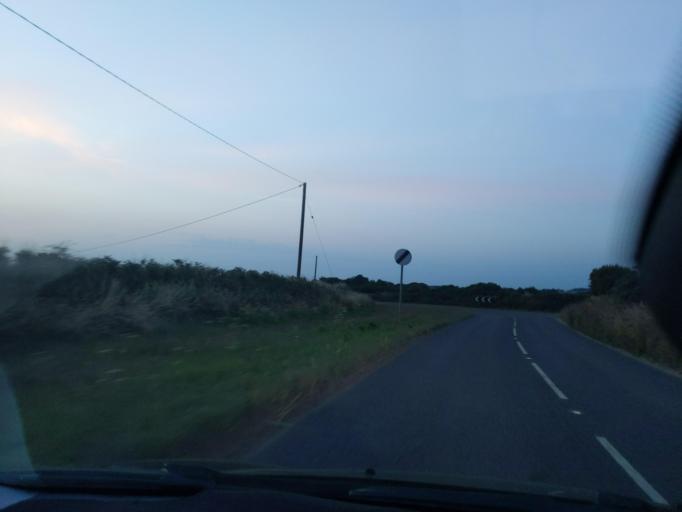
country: GB
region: England
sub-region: Cornwall
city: Camborne
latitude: 50.1821
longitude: -5.3120
